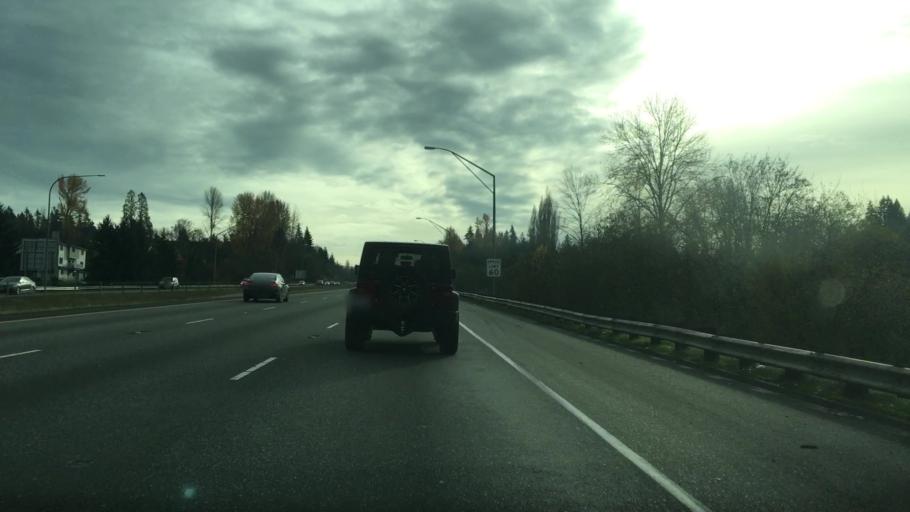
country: US
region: Washington
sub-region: Pierce County
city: Puyallup
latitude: 47.1721
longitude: -122.2971
